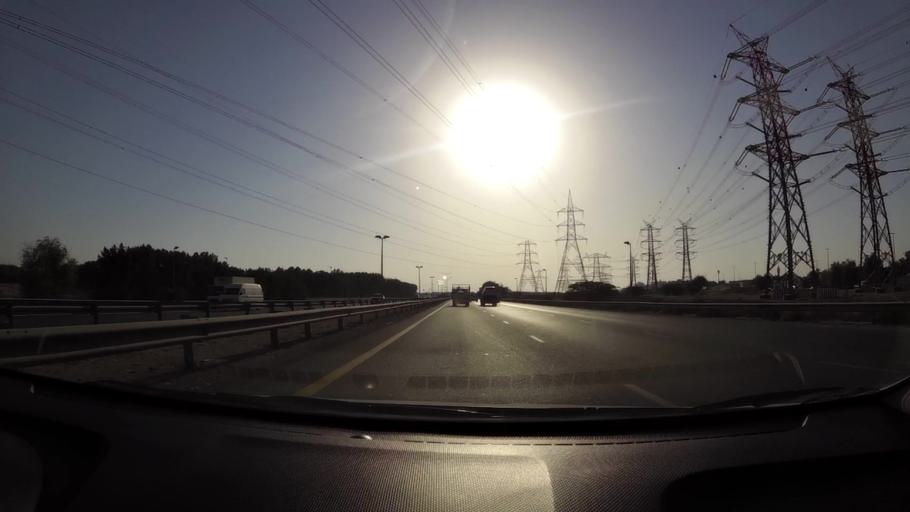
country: AE
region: Ajman
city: Ajman
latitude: 25.3584
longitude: 55.4920
